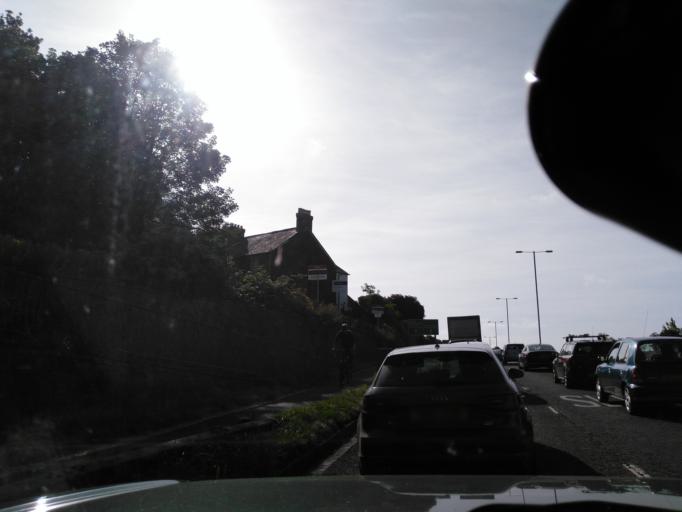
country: GB
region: England
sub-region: Wiltshire
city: Salisbury
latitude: 51.0759
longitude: -1.7905
